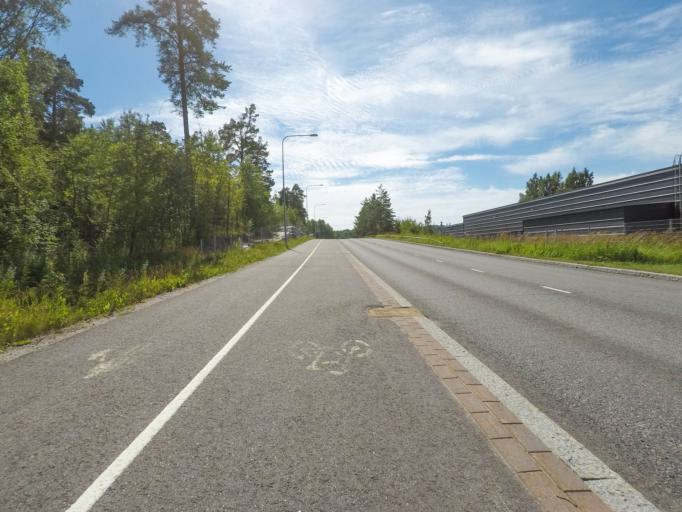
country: FI
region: Uusimaa
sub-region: Helsinki
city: Vantaa
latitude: 60.2125
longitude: 25.0678
